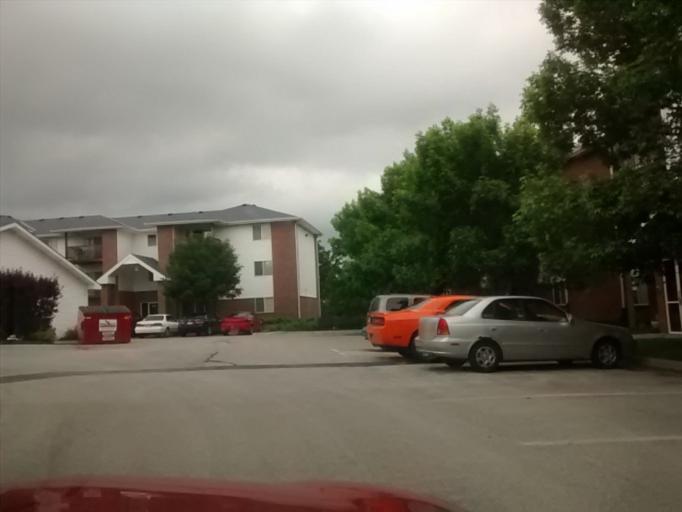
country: US
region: Nebraska
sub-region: Sarpy County
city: Offutt Air Force Base
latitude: 41.1607
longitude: -95.9433
